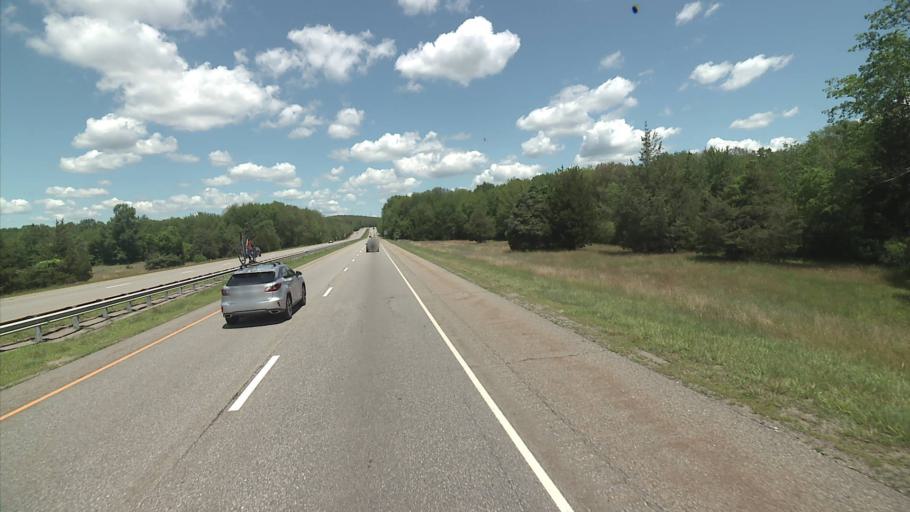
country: US
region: Connecticut
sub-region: Windham County
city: Plainfield
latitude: 41.6763
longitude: -71.9087
